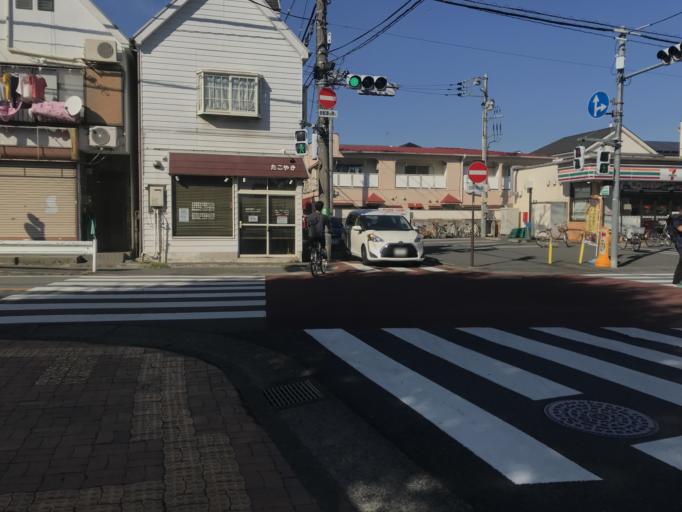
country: JP
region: Tokyo
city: Higashimurayama-shi
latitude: 35.7444
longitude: 139.4632
